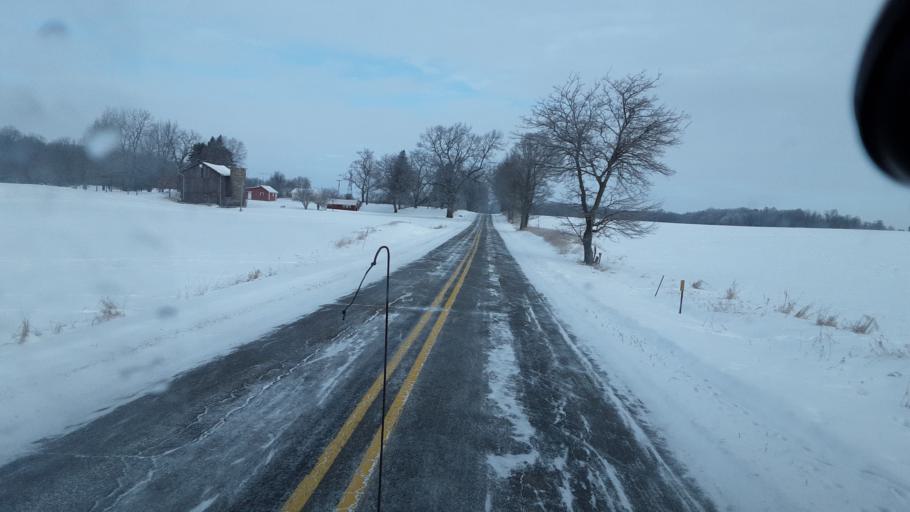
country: US
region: Michigan
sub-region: Ingham County
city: Leslie
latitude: 42.3529
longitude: -84.4826
